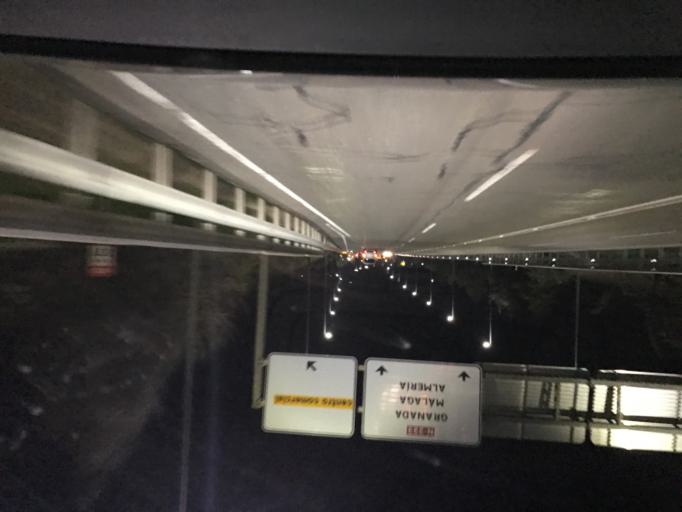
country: ES
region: Andalusia
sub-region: Provincia de Jaen
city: Jaen
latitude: 37.7858
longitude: -3.7700
